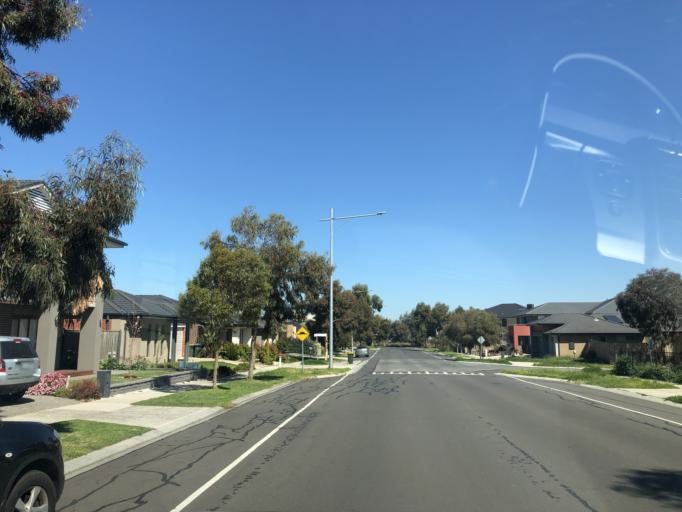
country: AU
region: Victoria
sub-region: Wyndham
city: Hoppers Crossing
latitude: -37.8980
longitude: 144.7241
